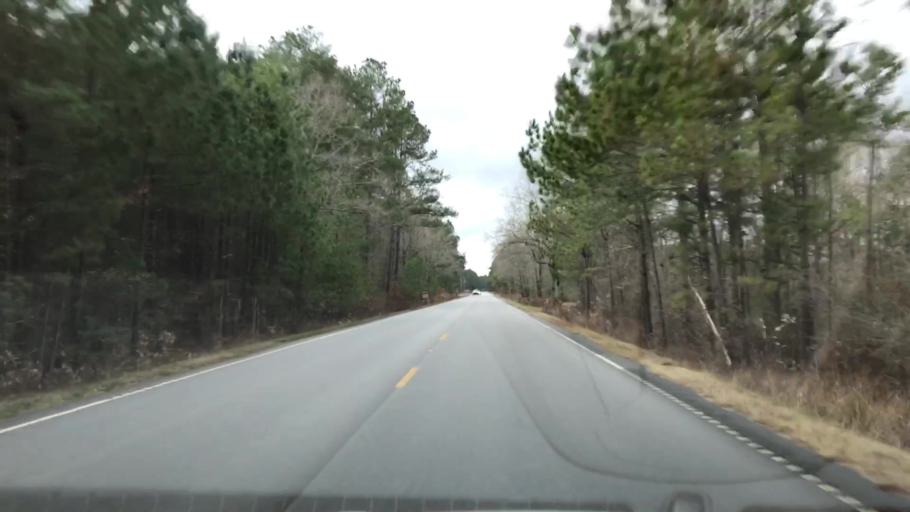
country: US
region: South Carolina
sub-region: Berkeley County
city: Saint Stephen
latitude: 33.2876
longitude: -79.7611
